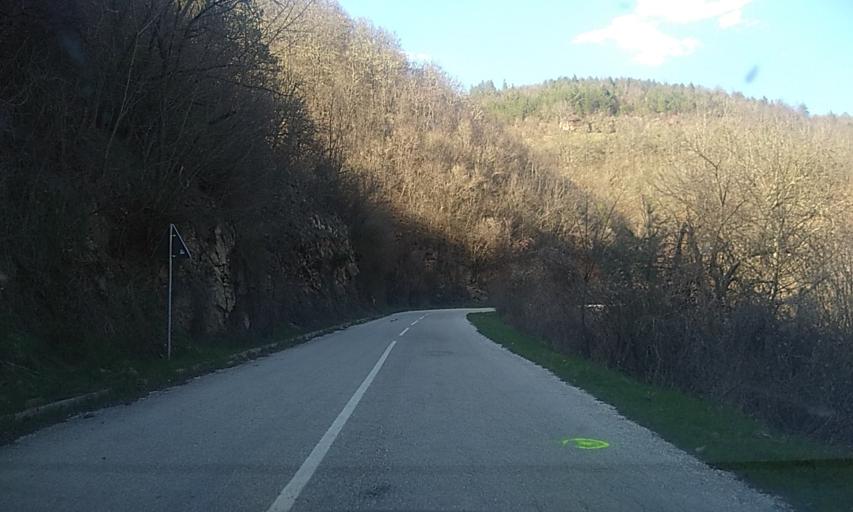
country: RS
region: Central Serbia
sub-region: Pcinjski Okrug
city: Bosilegrad
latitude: 42.4161
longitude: 22.5015
